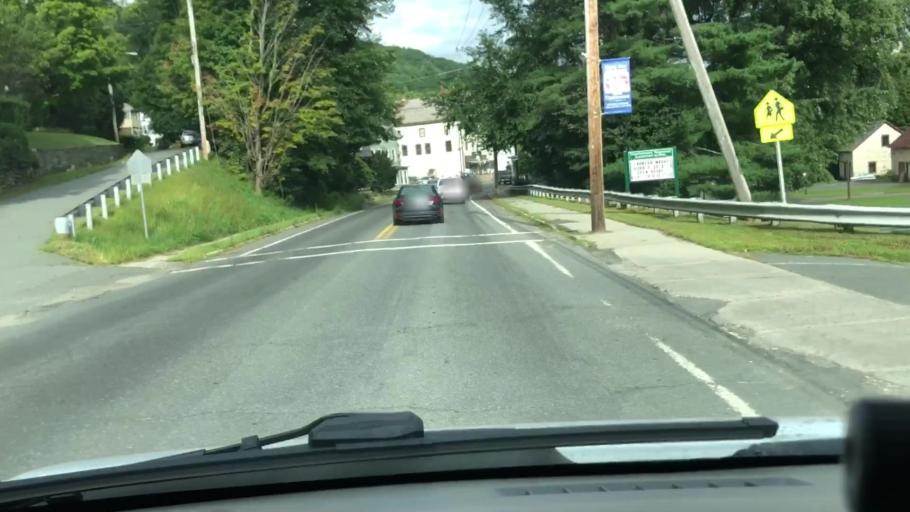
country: US
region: Massachusetts
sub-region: Franklin County
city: Charlemont
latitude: 42.6279
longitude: -72.8752
